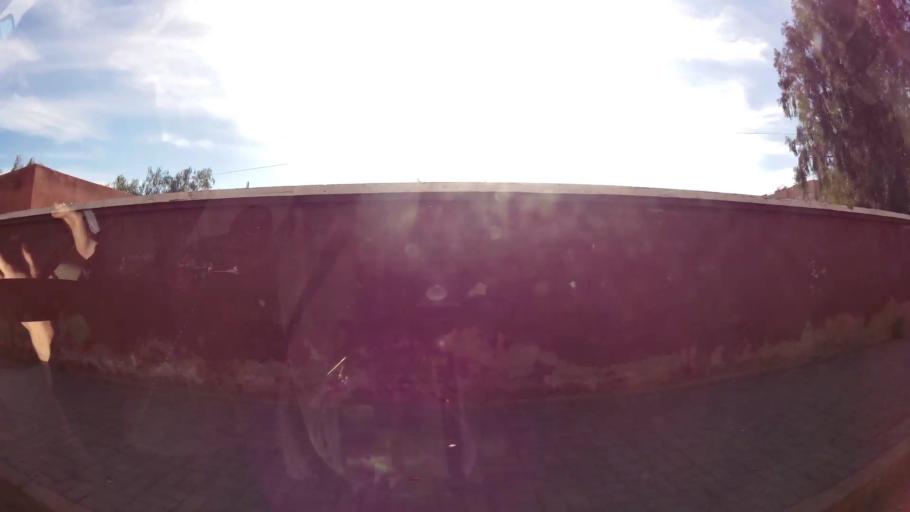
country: MA
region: Marrakech-Tensift-Al Haouz
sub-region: Marrakech
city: Marrakesh
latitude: 31.6860
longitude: -8.0623
